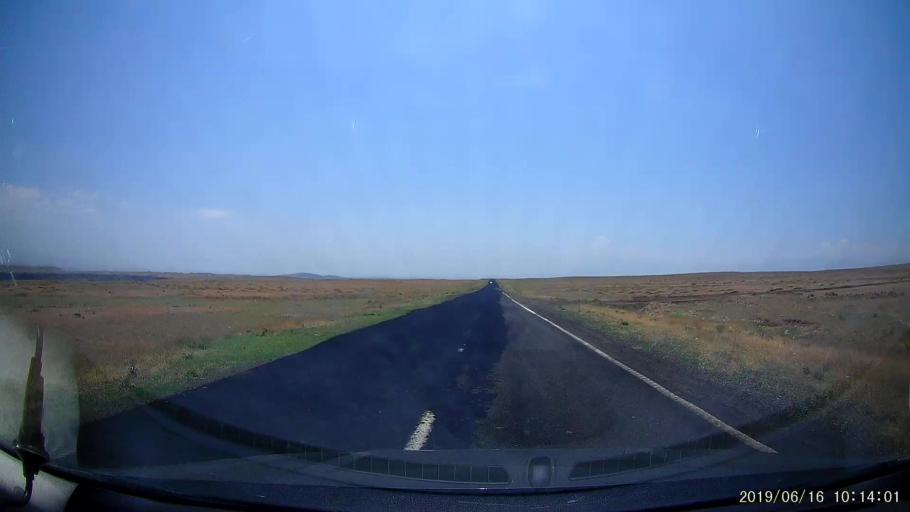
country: TR
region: Igdir
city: Tuzluca
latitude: 40.1884
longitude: 43.6543
